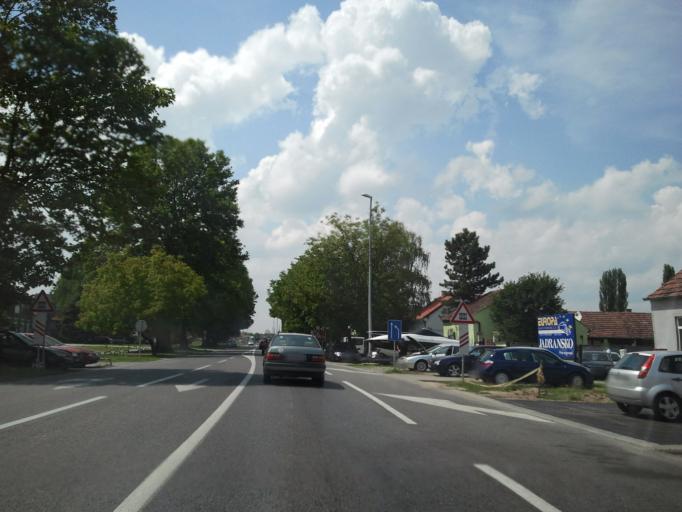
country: HR
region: Vukovarsko-Srijemska
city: Borovo
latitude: 45.3723
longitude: 18.9539
